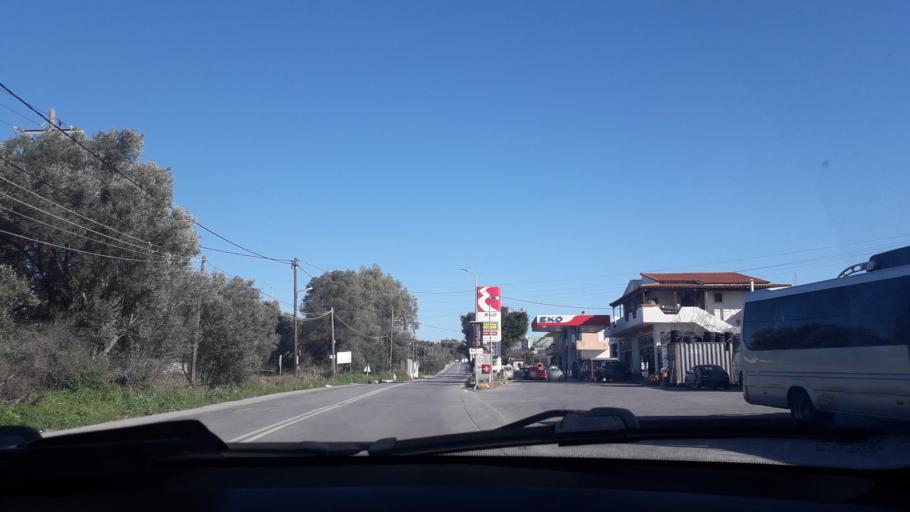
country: GR
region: Crete
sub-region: Nomos Rethymnis
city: Rethymno
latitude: 35.3612
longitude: 24.5455
